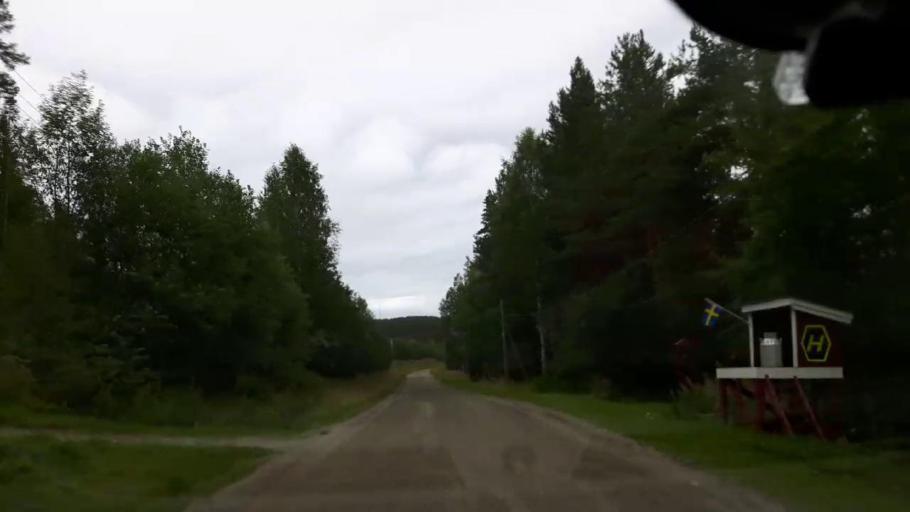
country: SE
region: Jaemtland
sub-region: Braecke Kommun
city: Braecke
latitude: 63.0130
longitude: 15.3784
